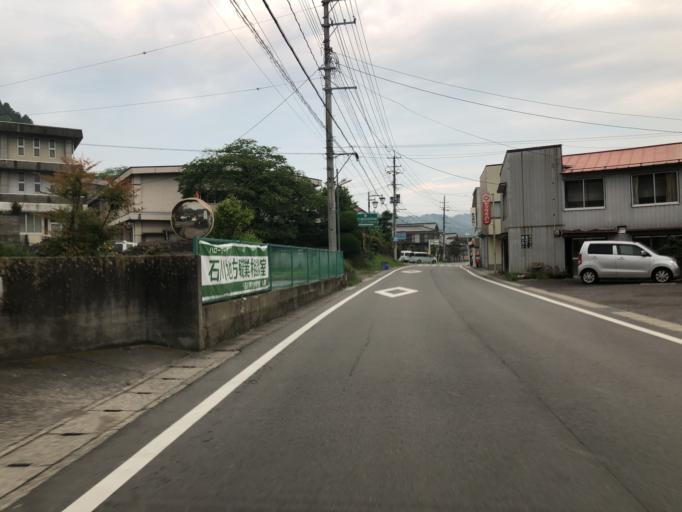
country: JP
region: Fukushima
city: Ishikawa
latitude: 37.1495
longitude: 140.4530
